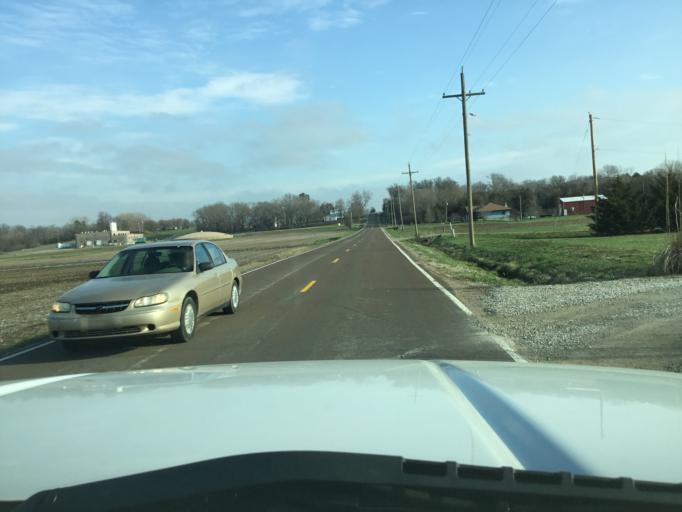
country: US
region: Kansas
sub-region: Shawnee County
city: Topeka
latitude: 39.1014
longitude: -95.7484
